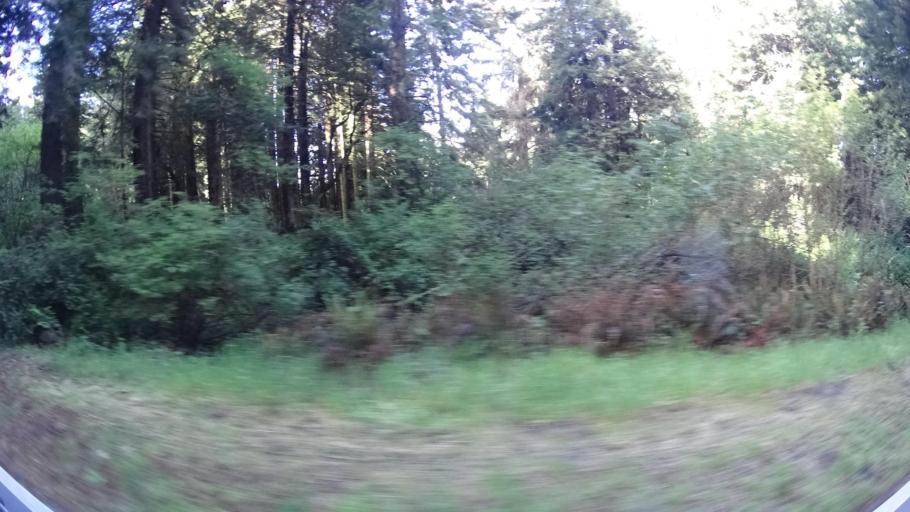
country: US
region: California
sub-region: Humboldt County
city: Westhaven-Moonstone
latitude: 41.0600
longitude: -124.1385
